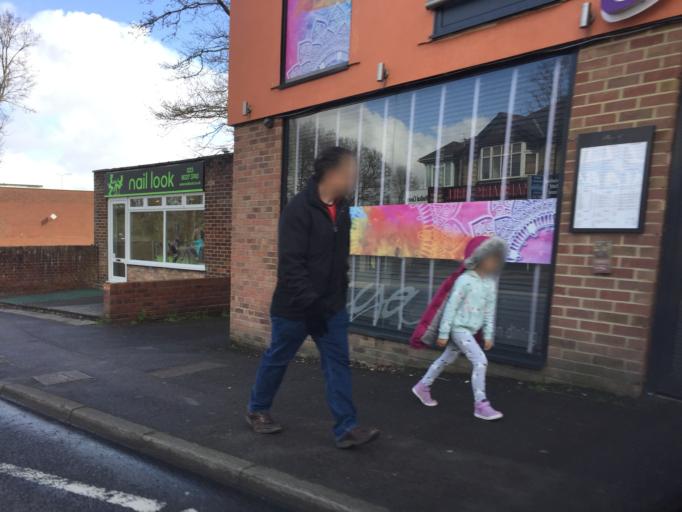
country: GB
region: England
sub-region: Hampshire
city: Chandlers Ford
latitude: 50.9821
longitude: -1.3835
